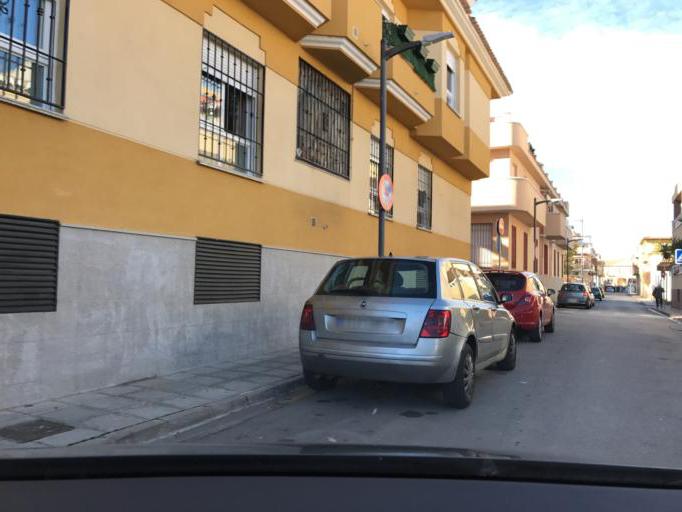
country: ES
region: Andalusia
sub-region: Provincia de Granada
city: Churriana de la Vega
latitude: 37.1481
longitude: -3.6502
